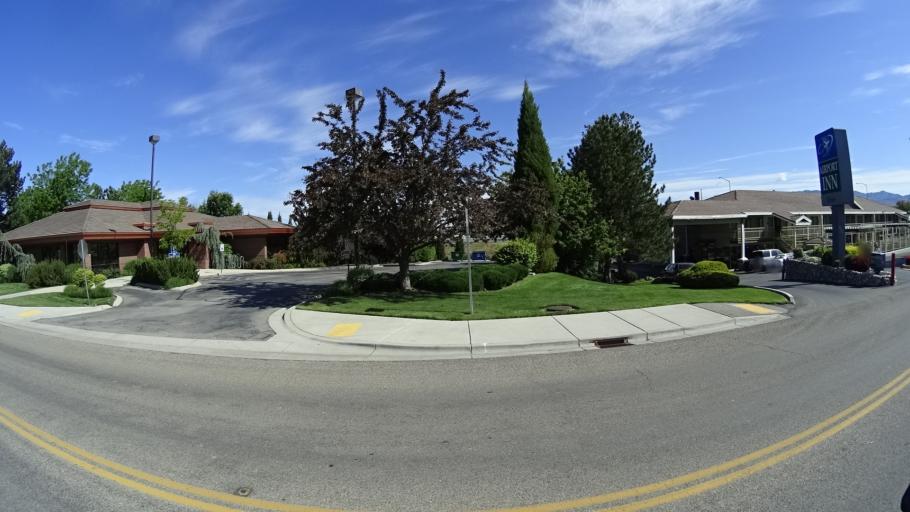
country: US
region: Idaho
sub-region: Ada County
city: Boise
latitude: 43.5694
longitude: -116.2147
